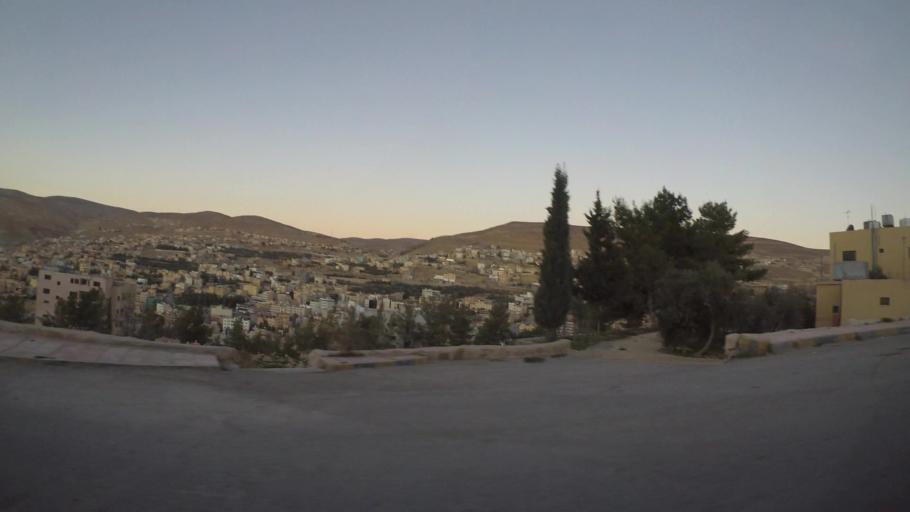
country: JO
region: Ma'an
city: Petra
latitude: 30.3183
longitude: 35.4747
